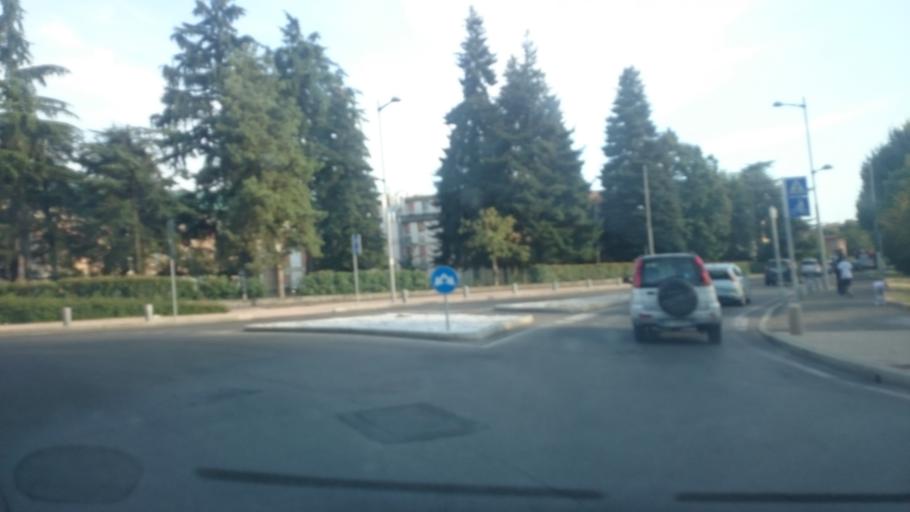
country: IT
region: Emilia-Romagna
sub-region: Provincia di Reggio Emilia
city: Reggio nell'Emilia
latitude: 44.6809
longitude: 10.6199
